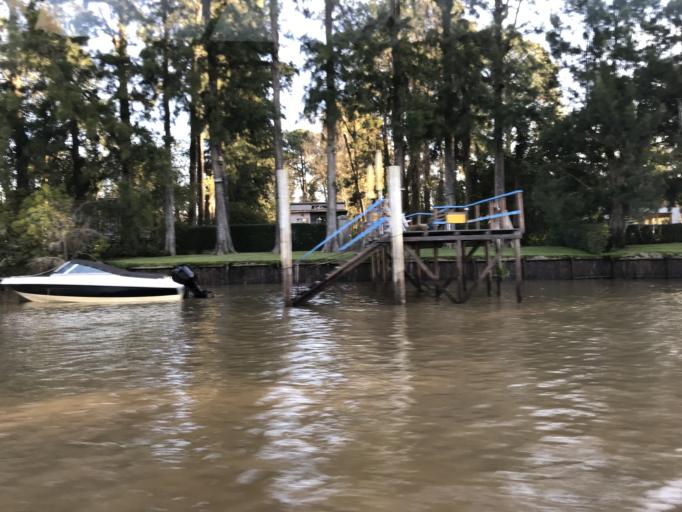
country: AR
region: Buenos Aires
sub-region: Partido de Tigre
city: Tigre
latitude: -34.3784
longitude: -58.5754
